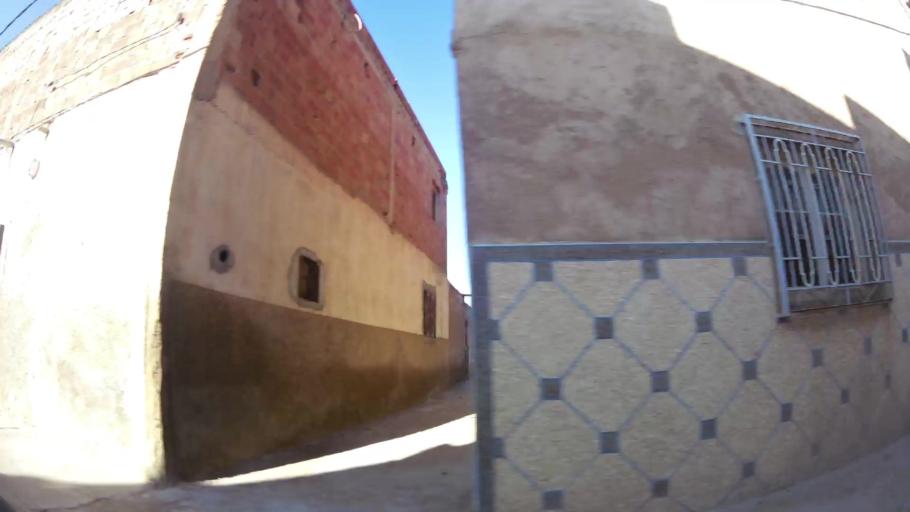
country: MA
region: Oriental
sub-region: Oujda-Angad
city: Oujda
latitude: 34.7227
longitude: -1.8919
